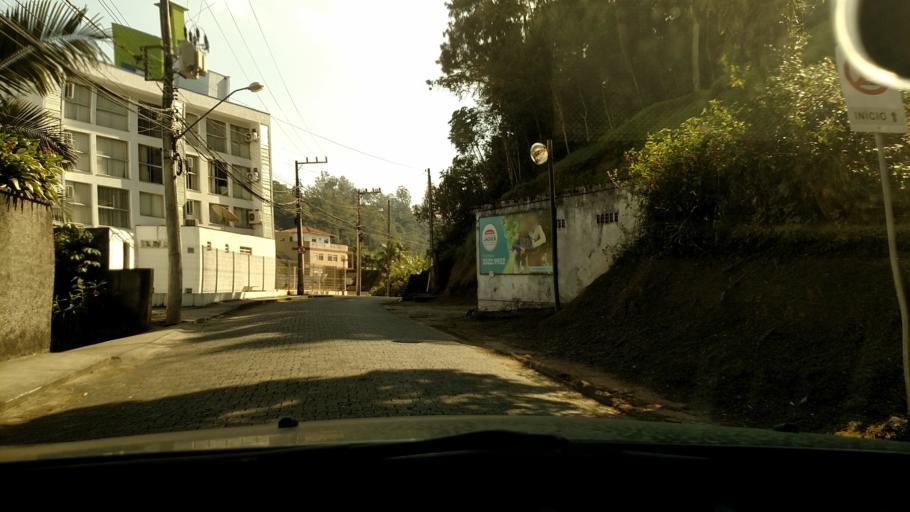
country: BR
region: Santa Catarina
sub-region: Blumenau
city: Blumenau
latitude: -26.9134
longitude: -49.0659
